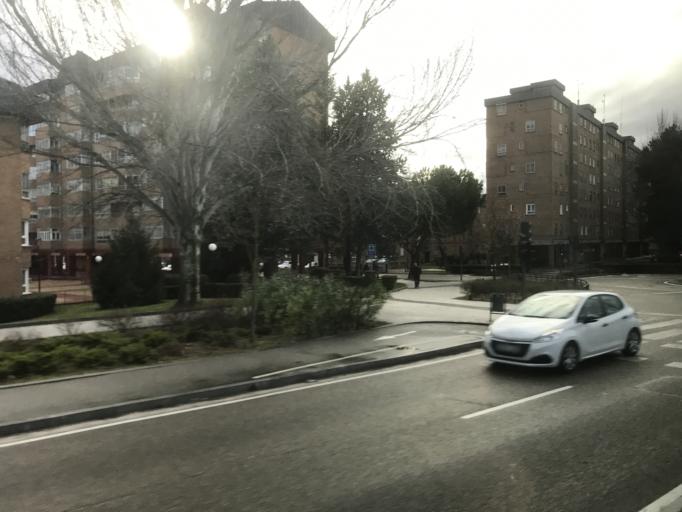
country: ES
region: Castille and Leon
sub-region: Provincia de Valladolid
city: Valladolid
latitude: 41.6466
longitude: -4.7390
